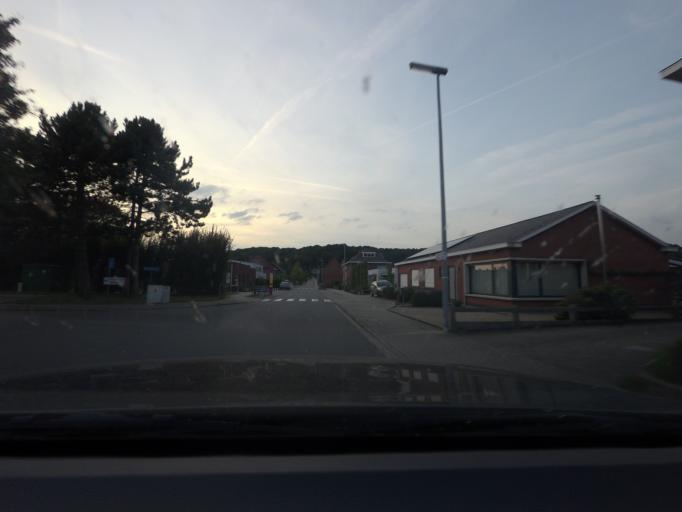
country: BE
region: Flanders
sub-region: Provincie Vlaams-Brabant
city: Holsbeek
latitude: 50.9007
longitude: 4.7328
